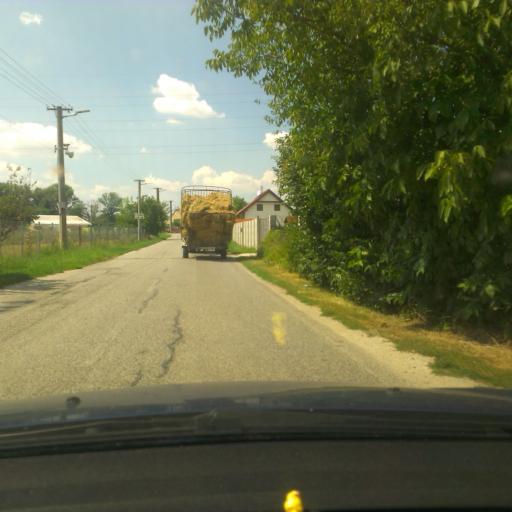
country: SK
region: Trnavsky
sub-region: Okres Trnava
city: Piestany
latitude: 48.5363
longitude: 17.8375
